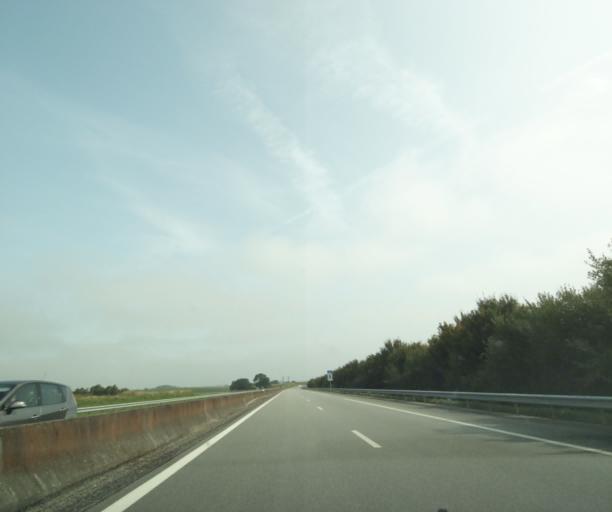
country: FR
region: Lower Normandy
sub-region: Departement de l'Orne
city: Sees
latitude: 48.5900
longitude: 0.1850
